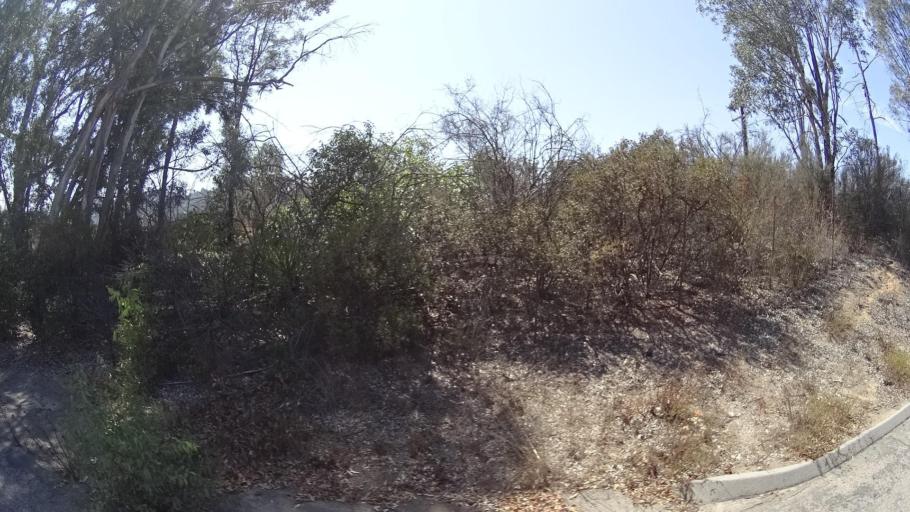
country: US
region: California
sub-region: San Diego County
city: Hidden Meadows
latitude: 33.2277
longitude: -117.0758
